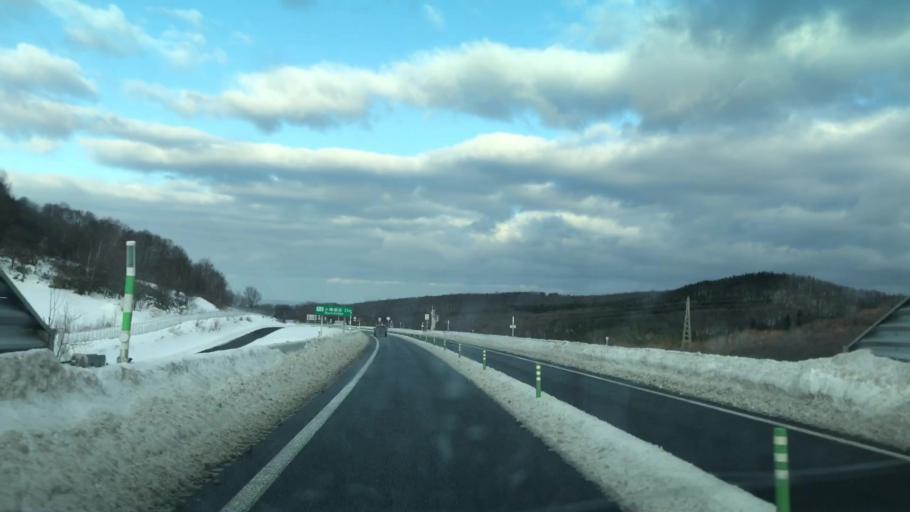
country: JP
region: Hokkaido
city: Otaru
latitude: 43.1953
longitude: 140.9528
